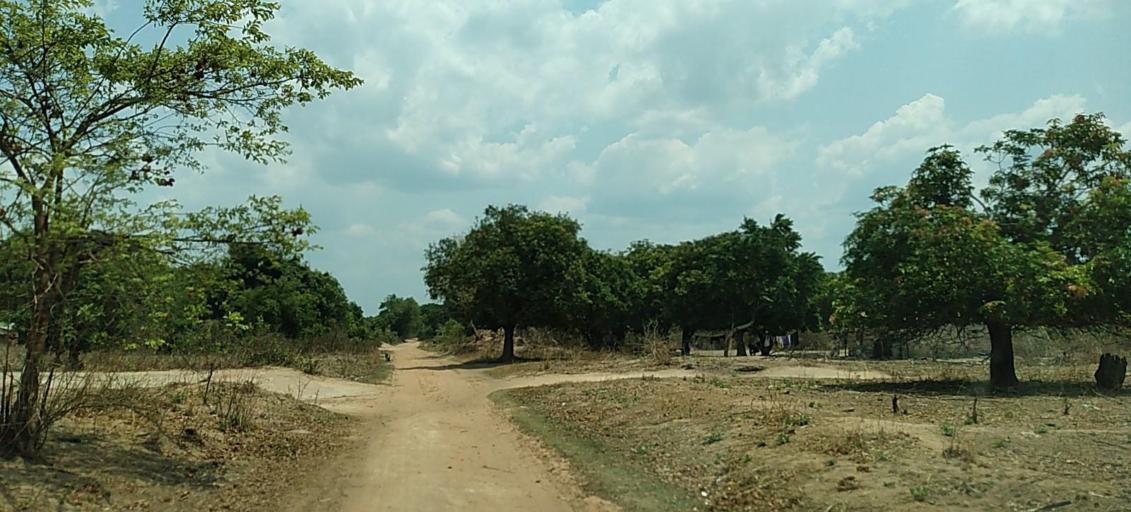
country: ZM
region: Copperbelt
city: Luanshya
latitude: -13.1637
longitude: 28.3063
